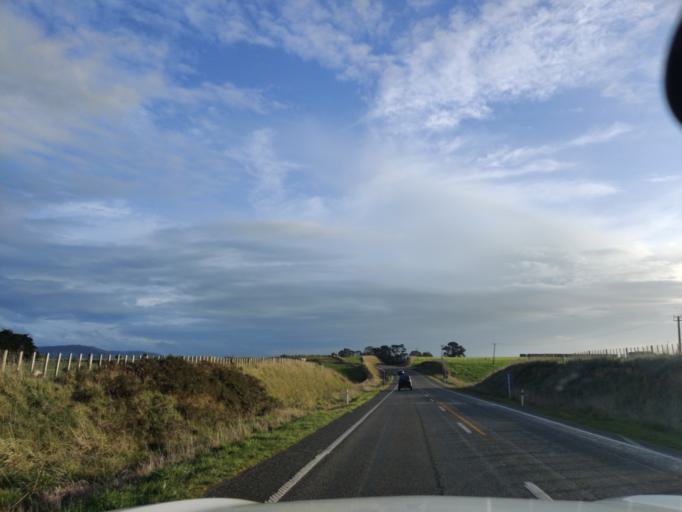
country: NZ
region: Manawatu-Wanganui
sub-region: Horowhenua District
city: Foxton
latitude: -40.5105
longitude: 175.4698
